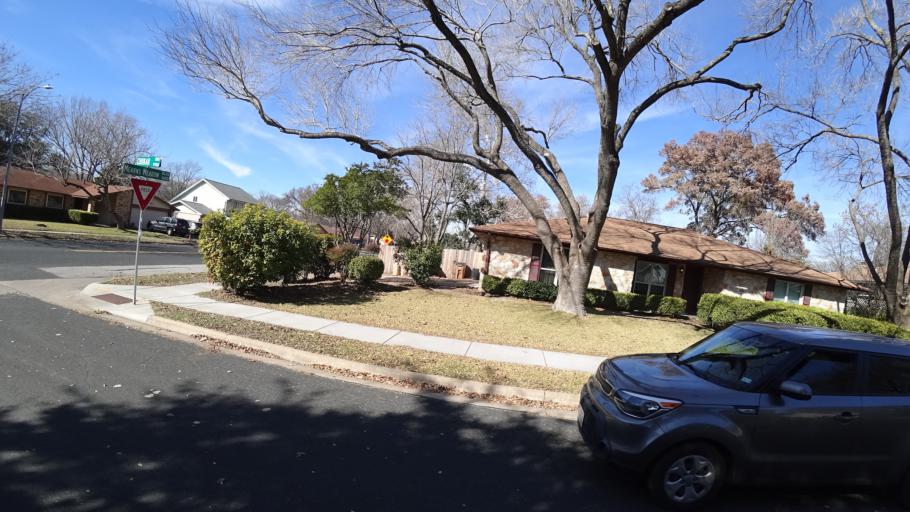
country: US
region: Texas
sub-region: Travis County
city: Wells Branch
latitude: 30.3748
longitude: -97.7042
